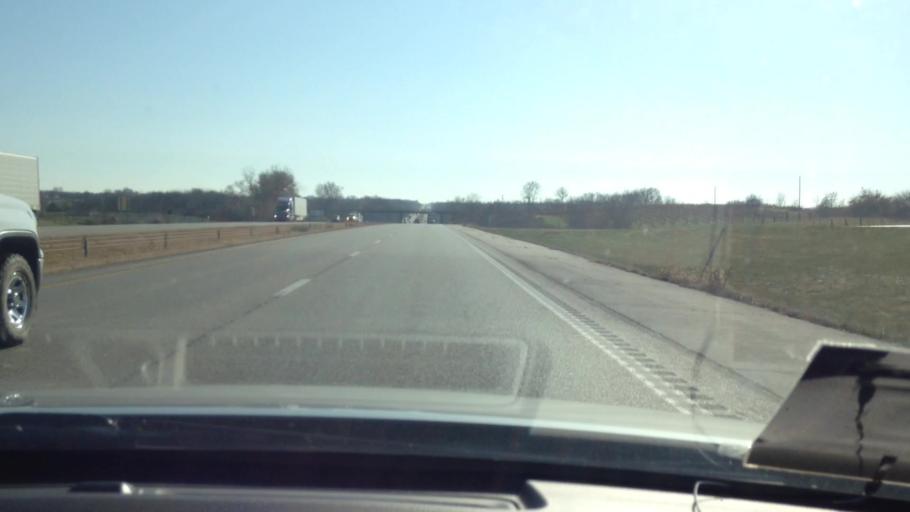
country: US
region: Missouri
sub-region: Platte County
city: Platte City
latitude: 39.4750
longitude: -94.7875
